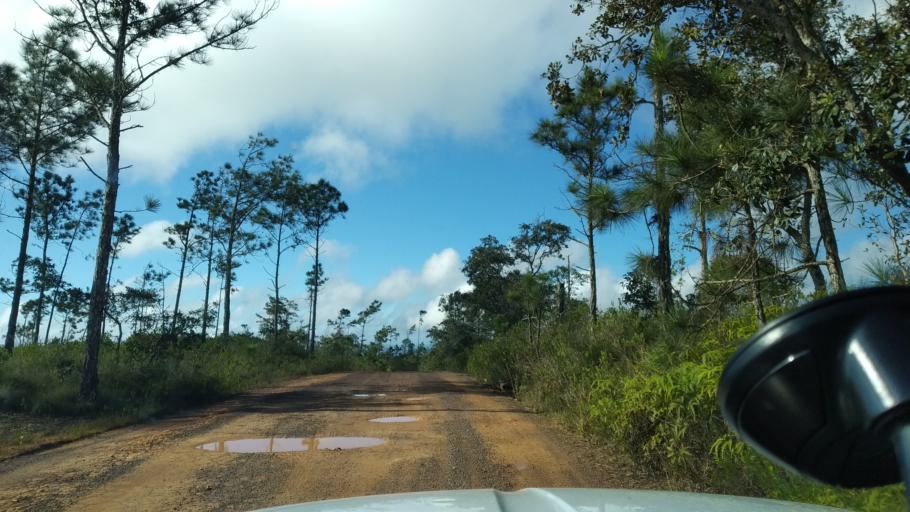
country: BZ
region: Cayo
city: Belmopan
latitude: 16.9969
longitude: -88.8267
